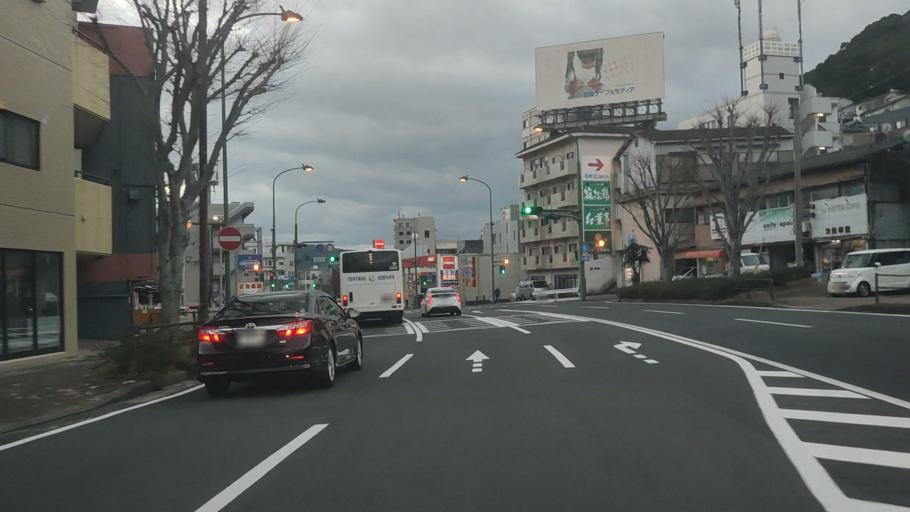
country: JP
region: Nagasaki
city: Nagasaki-shi
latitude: 32.7637
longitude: 129.8891
